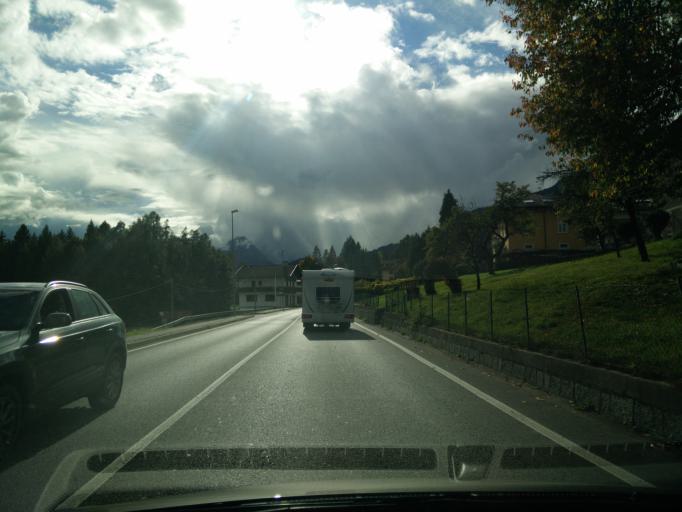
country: IT
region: Veneto
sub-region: Provincia di Belluno
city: Domegge di Cadore
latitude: 46.4559
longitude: 12.4076
